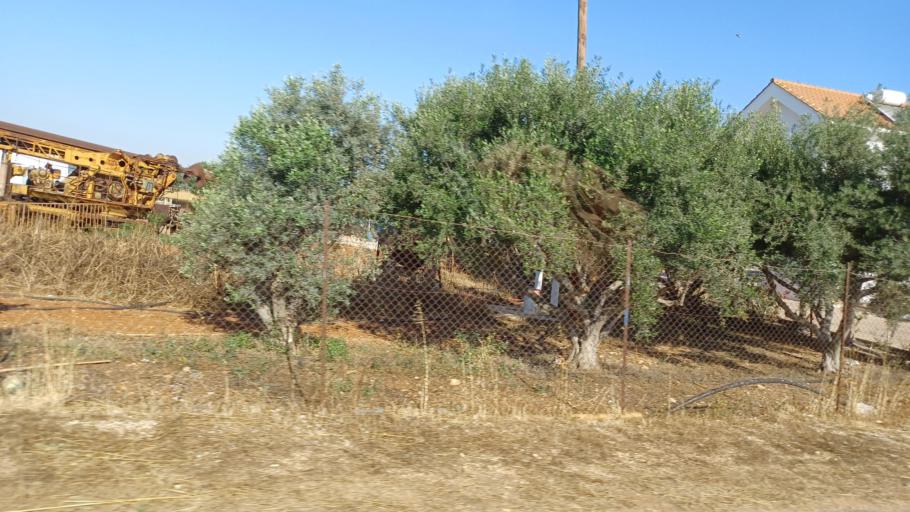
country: CY
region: Ammochostos
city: Frenaros
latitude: 35.0506
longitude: 33.9219
